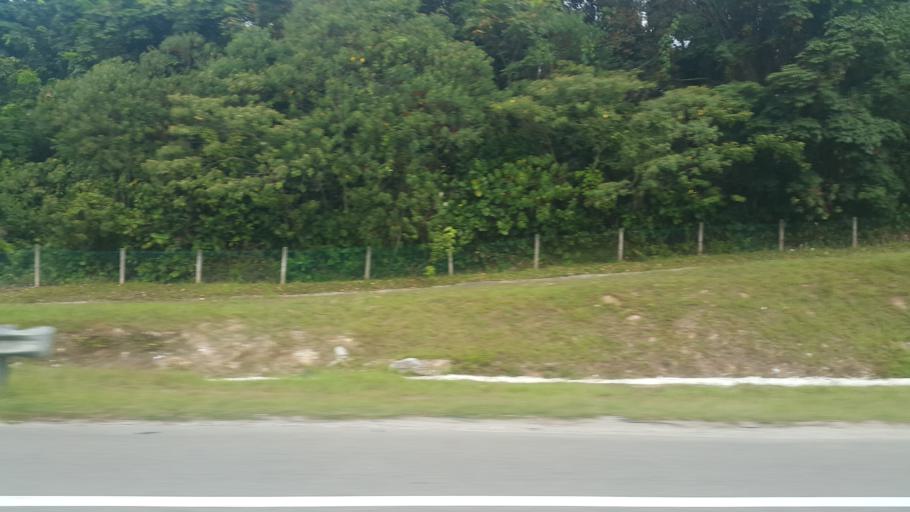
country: MY
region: Johor
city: Pekan Nenas
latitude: 1.4220
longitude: 103.6005
